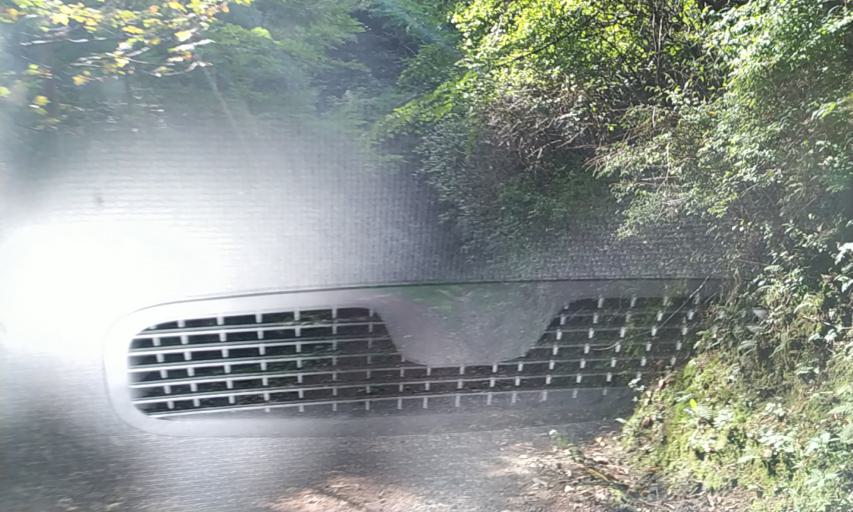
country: IT
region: Piedmont
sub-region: Provincia di Biella
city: Portula
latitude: 45.6815
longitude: 8.1722
